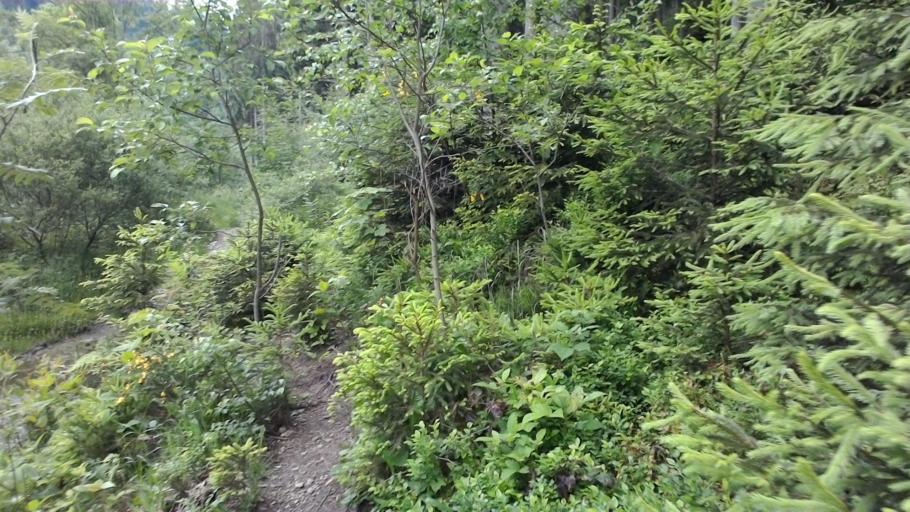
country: DE
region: North Rhine-Westphalia
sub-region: Regierungsbezirk Koln
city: Monschau
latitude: 50.5475
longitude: 6.2097
